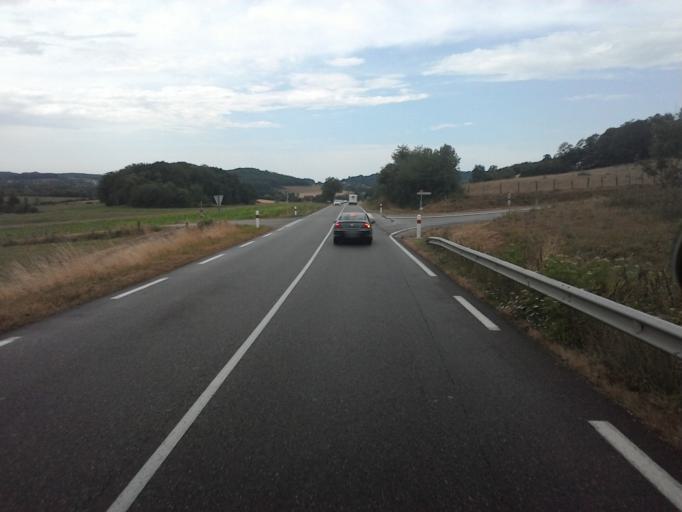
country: FR
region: Franche-Comte
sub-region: Departement du Jura
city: Poligny
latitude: 46.8243
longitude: 5.5952
